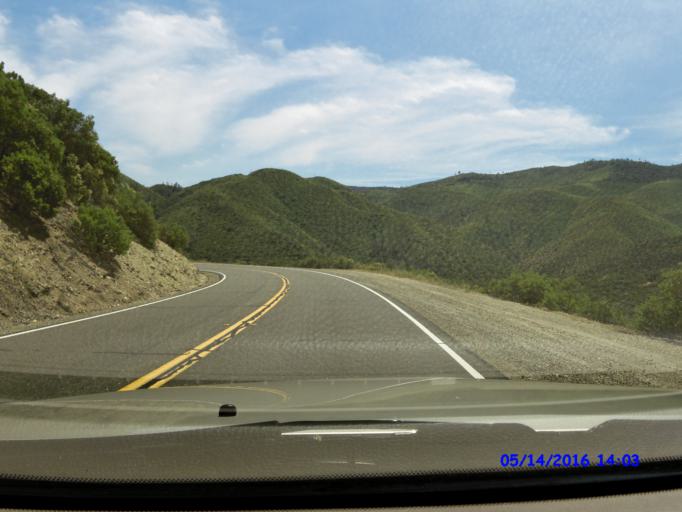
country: US
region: California
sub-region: Mariposa County
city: Mariposa
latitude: 37.5999
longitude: -120.1292
